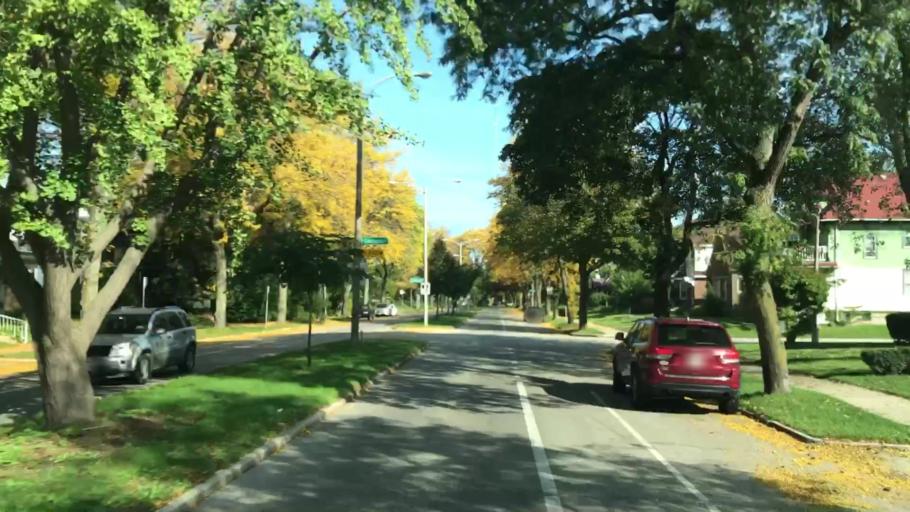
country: US
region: Wisconsin
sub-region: Milwaukee County
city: Shorewood
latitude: 43.0786
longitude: -87.8976
